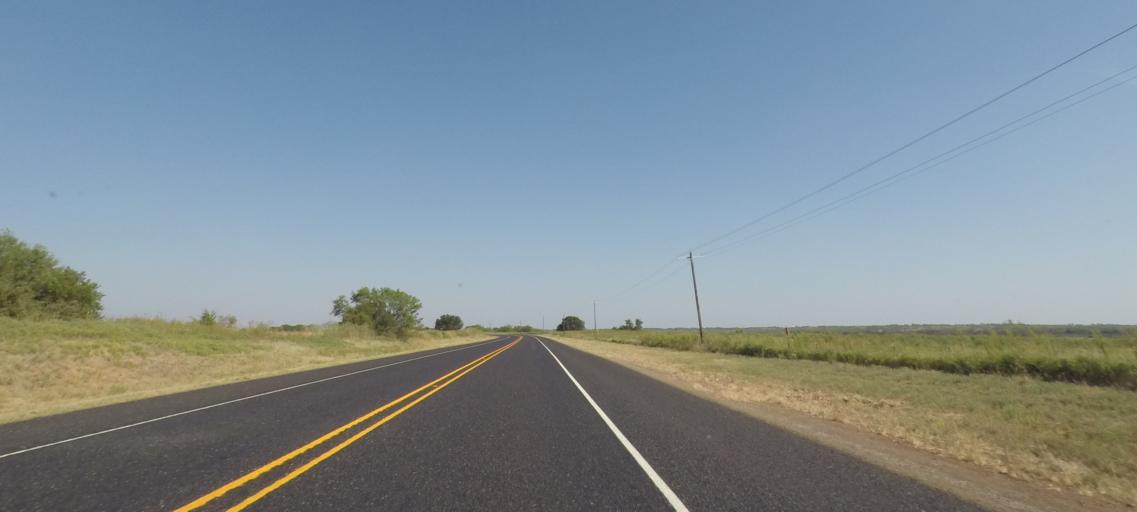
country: US
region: Texas
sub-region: Baylor County
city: Seymour
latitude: 33.5986
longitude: -99.3232
